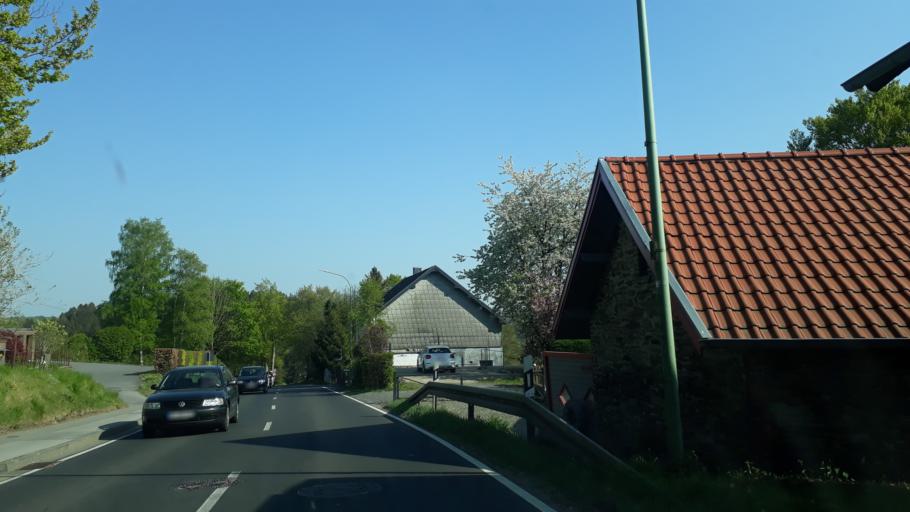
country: DE
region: North Rhine-Westphalia
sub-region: Regierungsbezirk Koln
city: Simmerath
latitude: 50.6280
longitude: 6.2865
